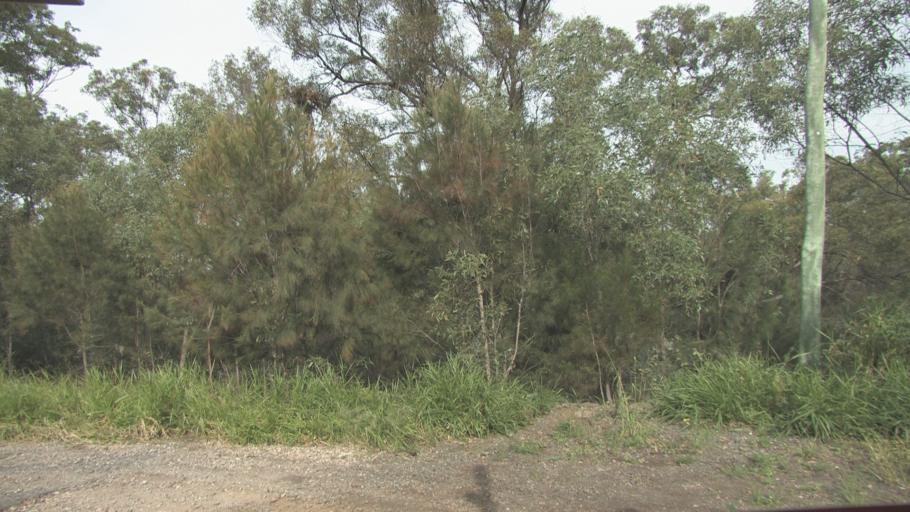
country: AU
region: Queensland
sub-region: Logan
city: Windaroo
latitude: -27.7293
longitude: 153.1589
